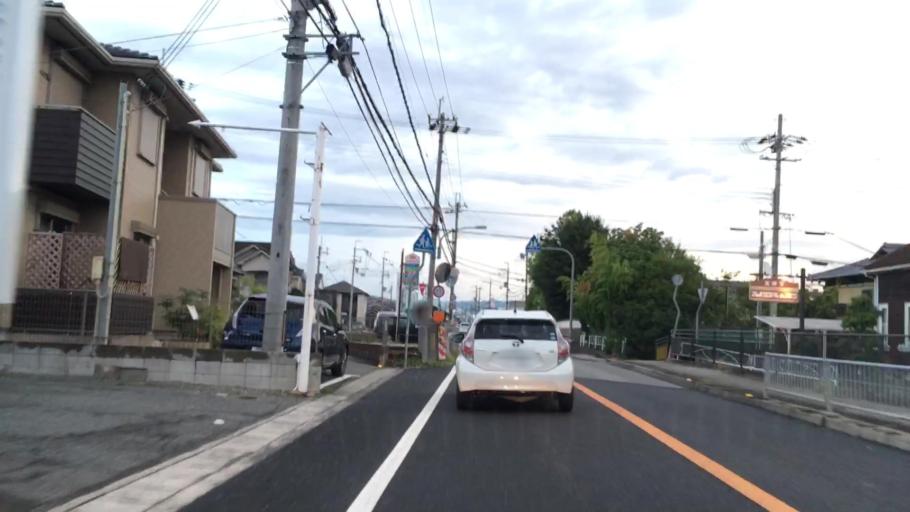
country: JP
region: Hyogo
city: Himeji
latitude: 34.9038
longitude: 134.7363
